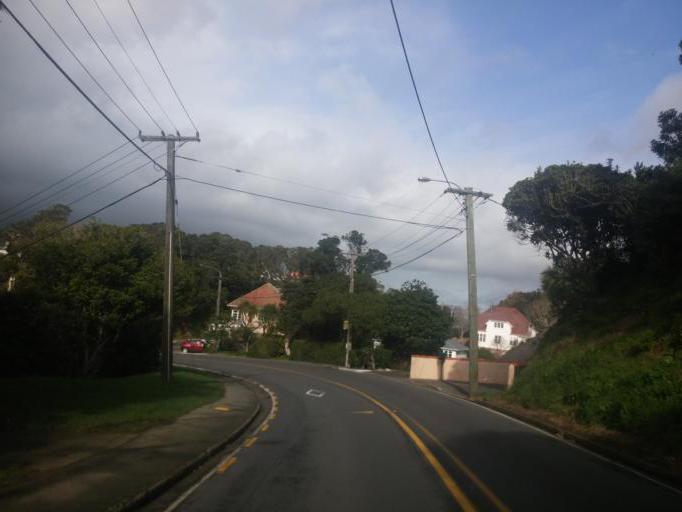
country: NZ
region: Wellington
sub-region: Wellington City
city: Kelburn
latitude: -41.2636
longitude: 174.7779
